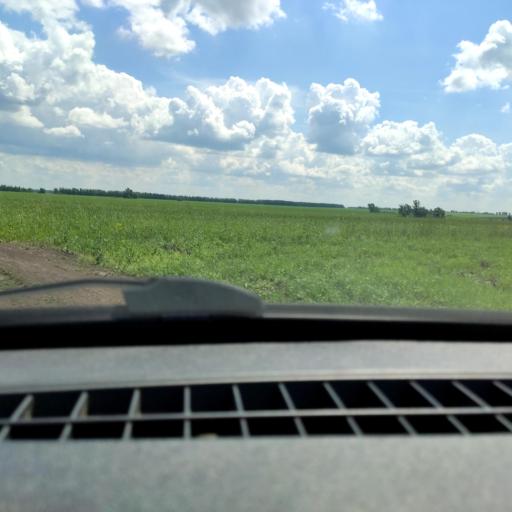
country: RU
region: Bashkortostan
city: Kabakovo
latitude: 54.5245
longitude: 56.0638
